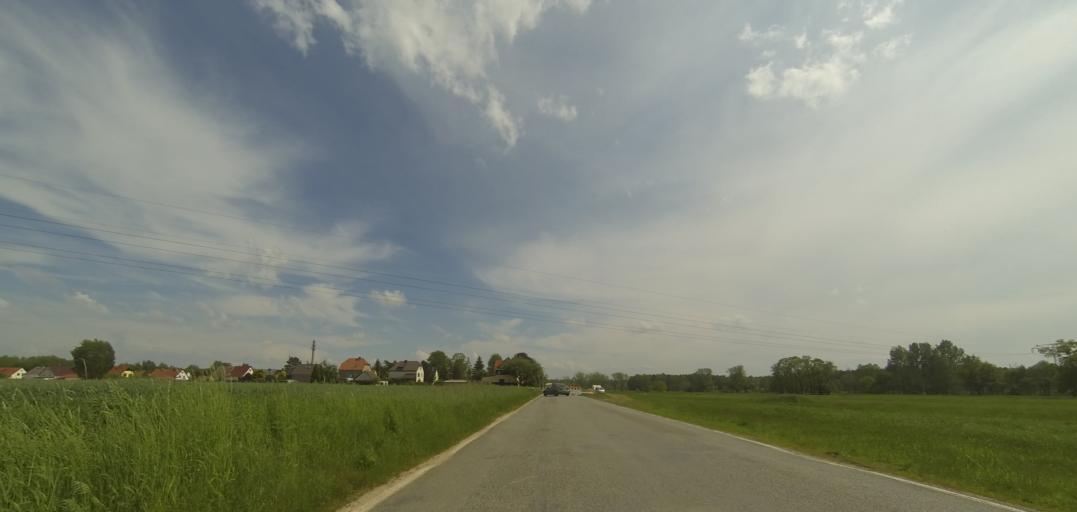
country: DE
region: Saxony
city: Arnsdorf
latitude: 51.0915
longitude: 13.9696
